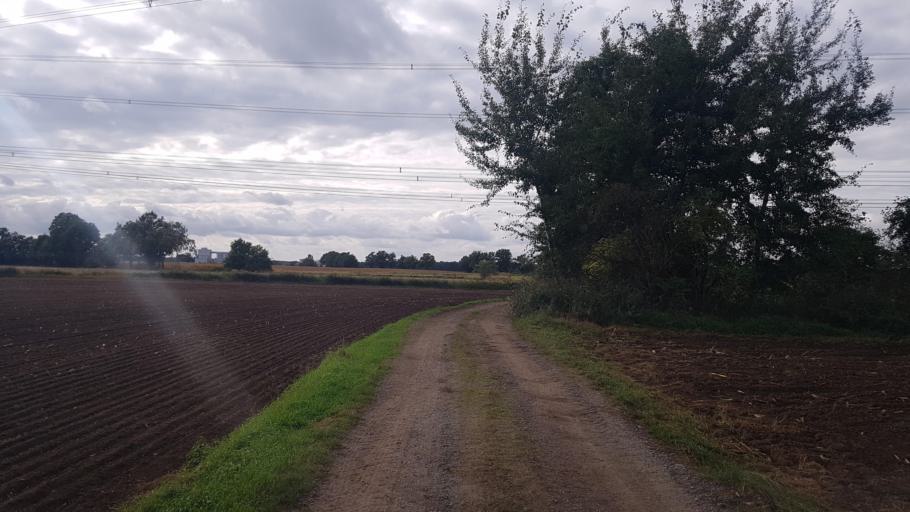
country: DE
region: Brandenburg
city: Bad Liebenwerda
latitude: 51.4849
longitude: 13.4104
